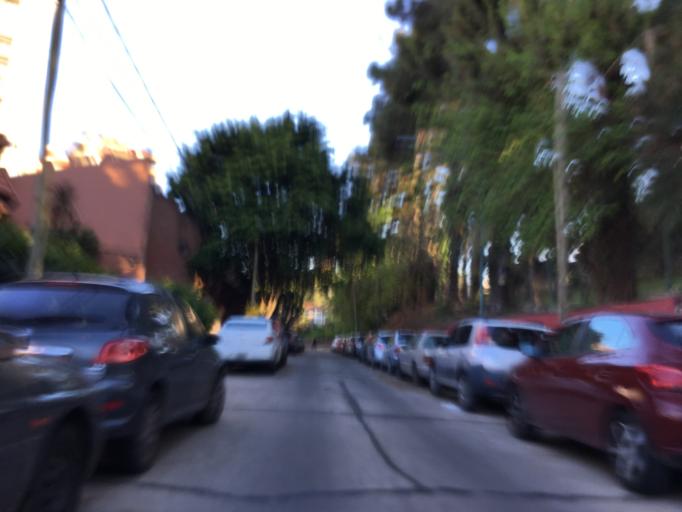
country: AR
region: Buenos Aires
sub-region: Partido de Vicente Lopez
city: Olivos
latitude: -34.5202
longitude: -58.4775
